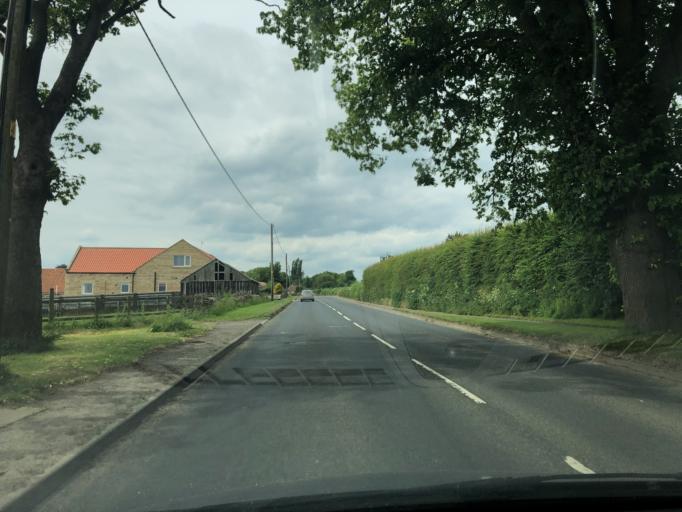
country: GB
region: England
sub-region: North Yorkshire
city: Pickering
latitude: 54.2591
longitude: -0.8041
